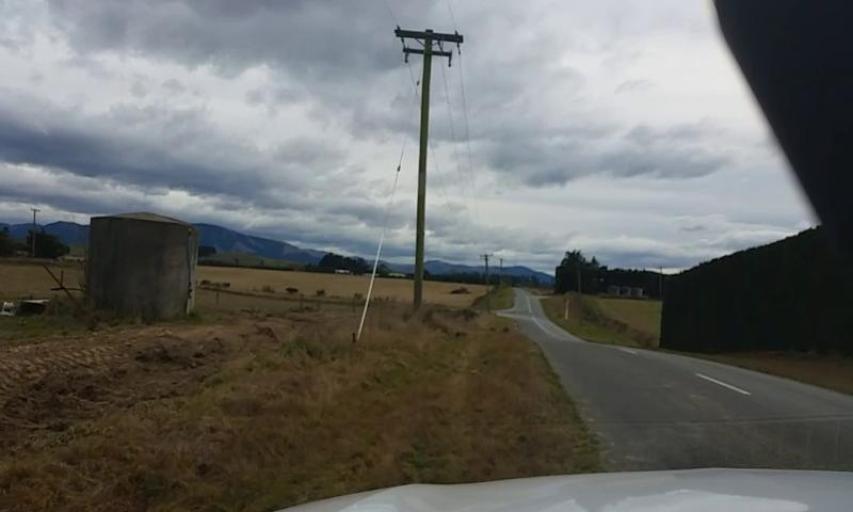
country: NZ
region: Canterbury
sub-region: Waimakariri District
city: Kaiapoi
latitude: -43.2928
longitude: 172.4374
